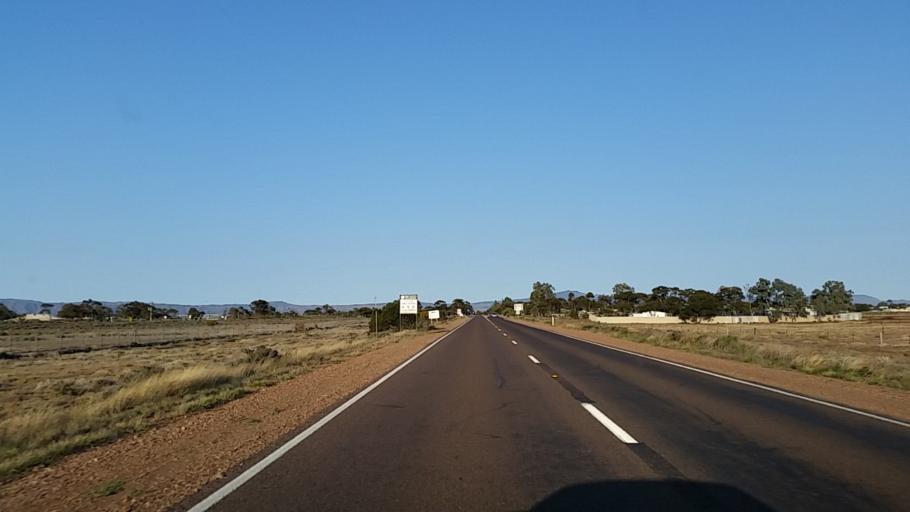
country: AU
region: South Australia
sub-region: Port Augusta
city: Port Augusta West
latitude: -32.4832
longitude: 137.7314
